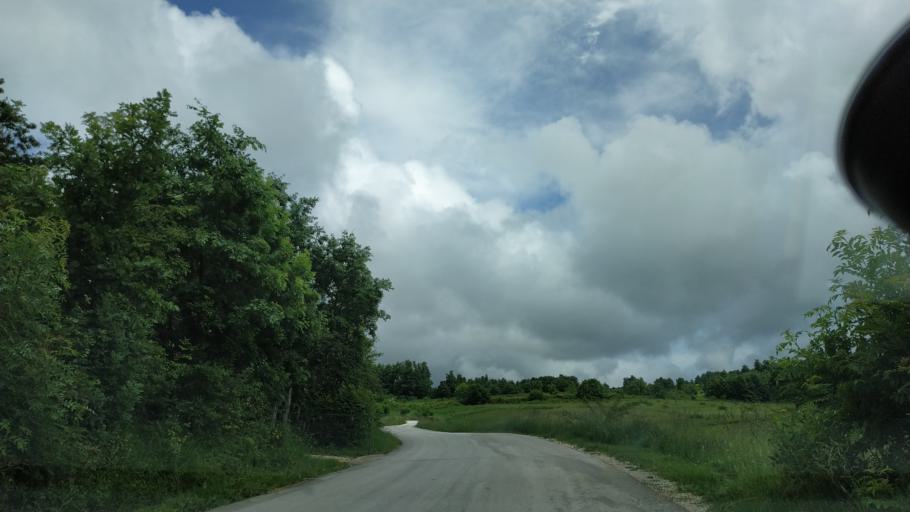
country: RS
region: Central Serbia
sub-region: Zajecarski Okrug
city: Soko Banja
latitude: 43.6841
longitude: 21.9313
